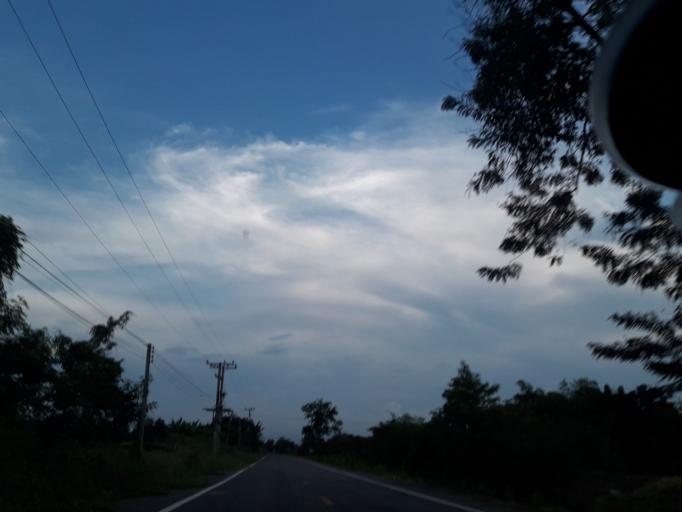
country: TH
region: Sara Buri
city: Nong Khae
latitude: 14.2431
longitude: 100.8689
